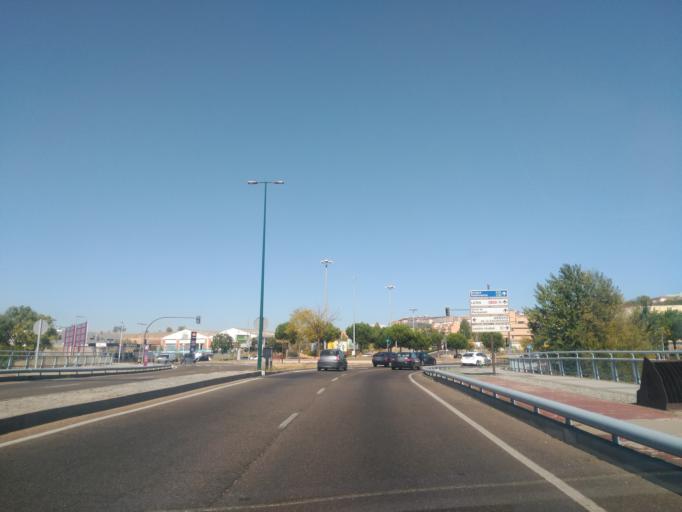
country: ES
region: Castille and Leon
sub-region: Provincia de Valladolid
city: Zaratan
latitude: 41.6268
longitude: -4.7579
